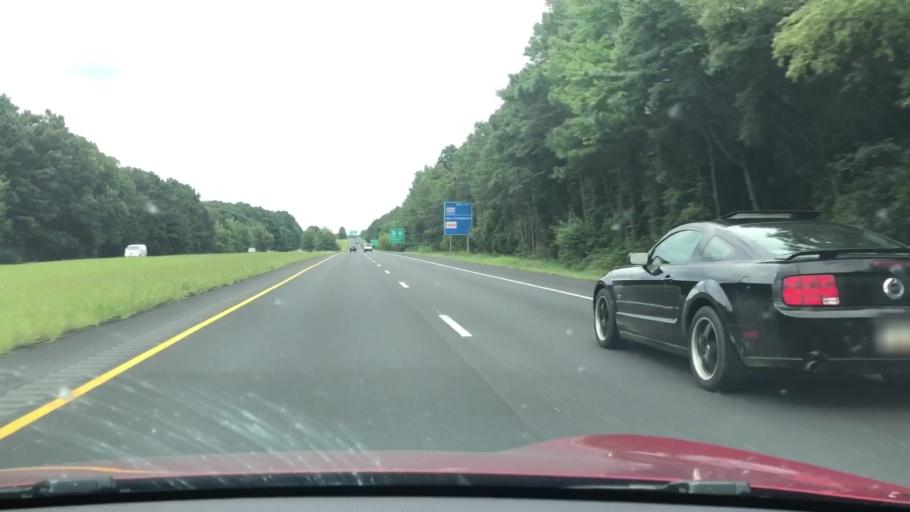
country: US
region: Maryland
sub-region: Wicomico County
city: Salisbury
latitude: 38.3483
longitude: -75.5432
